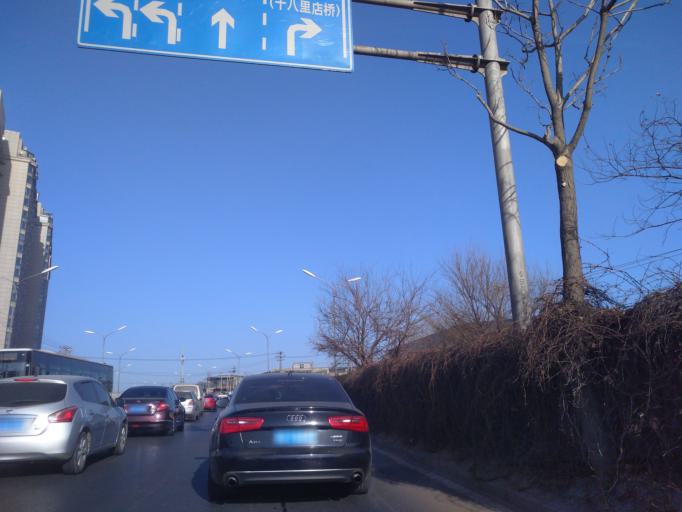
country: CN
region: Beijing
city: Jiugong
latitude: 39.8336
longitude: 116.4696
